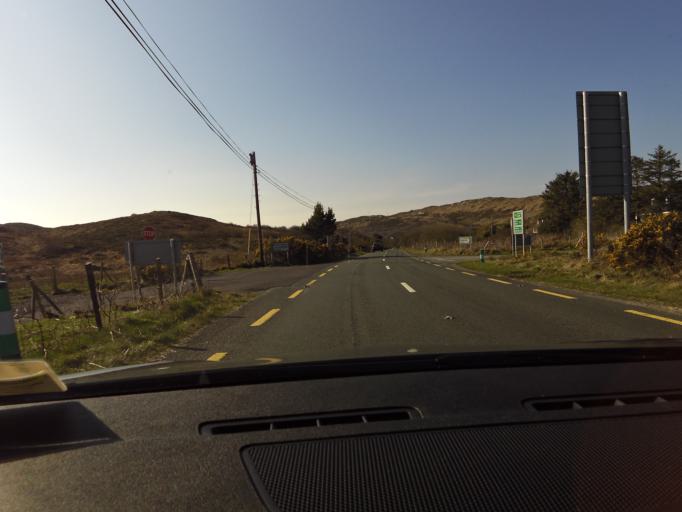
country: IE
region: Connaught
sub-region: County Galway
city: Clifden
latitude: 53.4839
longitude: -9.9778
